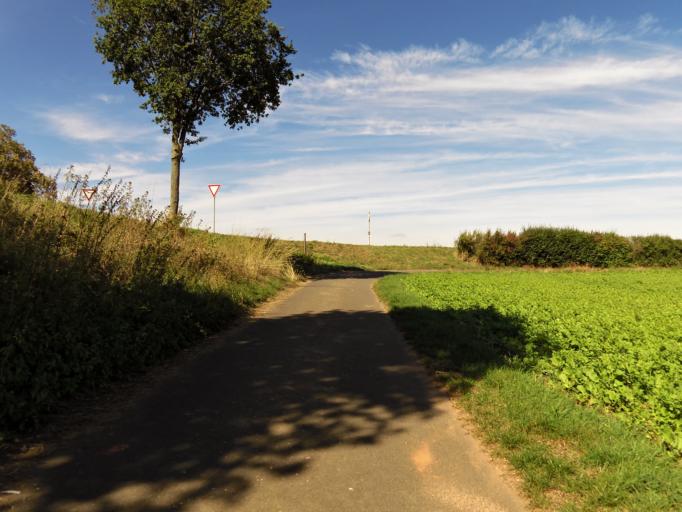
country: DE
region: Rheinland-Pfalz
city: Dreisen
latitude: 49.5968
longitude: 7.9986
